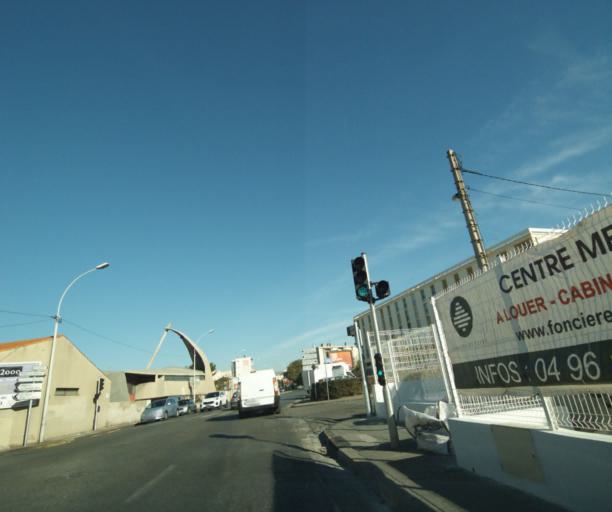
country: FR
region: Provence-Alpes-Cote d'Azur
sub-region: Departement des Bouches-du-Rhone
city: Marseille 10
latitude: 43.2765
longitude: 5.4186
